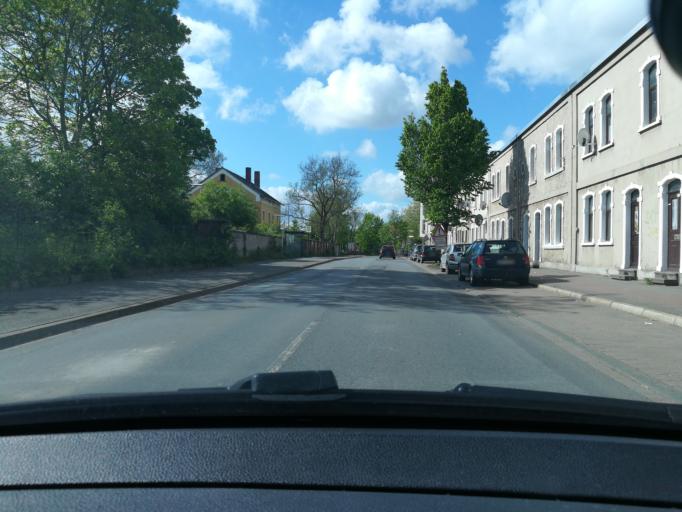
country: DE
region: North Rhine-Westphalia
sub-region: Regierungsbezirk Detmold
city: Minden
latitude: 52.2944
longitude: 8.9342
